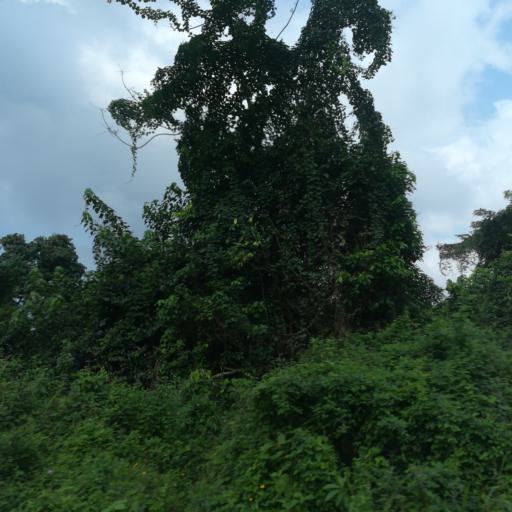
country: NG
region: Rivers
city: Okrika
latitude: 4.8325
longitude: 7.1270
